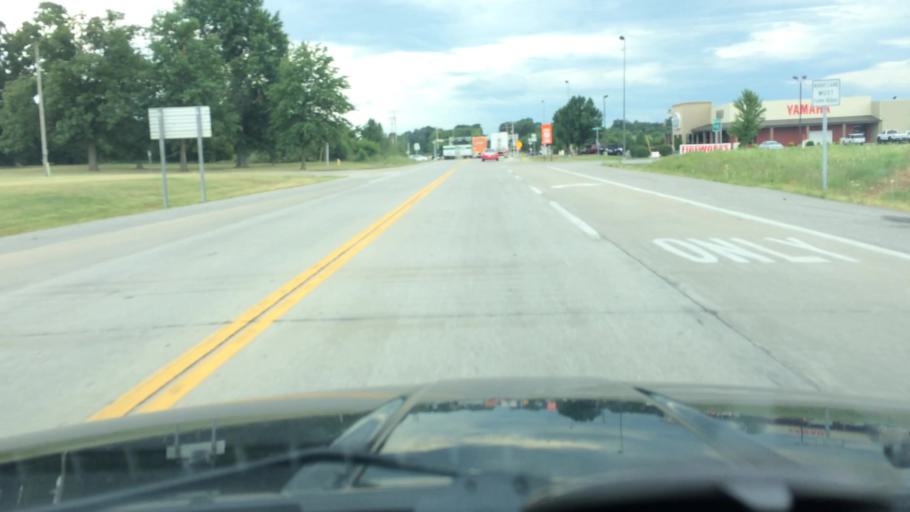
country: US
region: Missouri
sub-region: Greene County
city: Strafford
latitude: 37.2496
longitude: -93.1834
